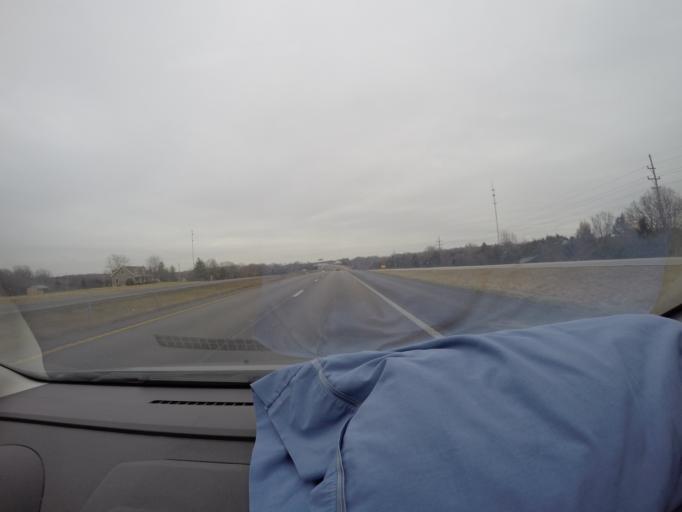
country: US
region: Missouri
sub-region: Warren County
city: Warrenton
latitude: 38.8223
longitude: -91.1931
